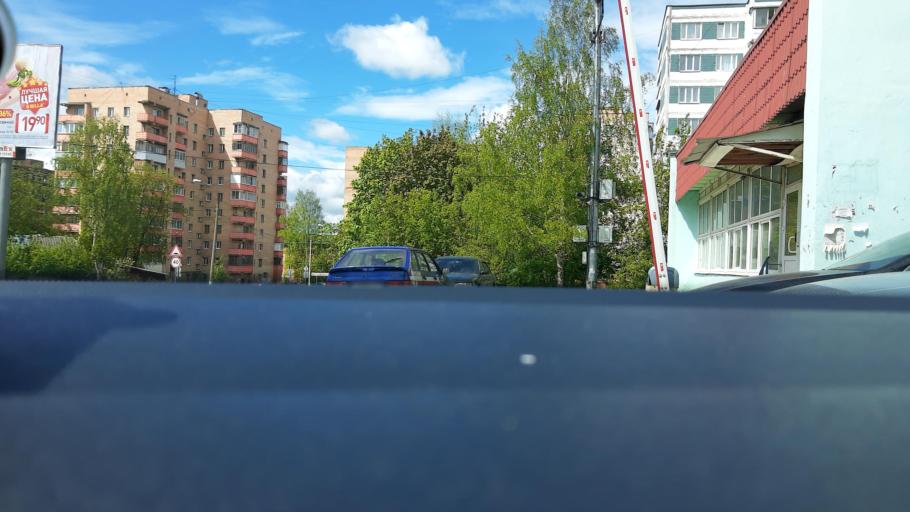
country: RU
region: Moskovskaya
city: Dmitrov
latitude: 56.3364
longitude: 37.5179
